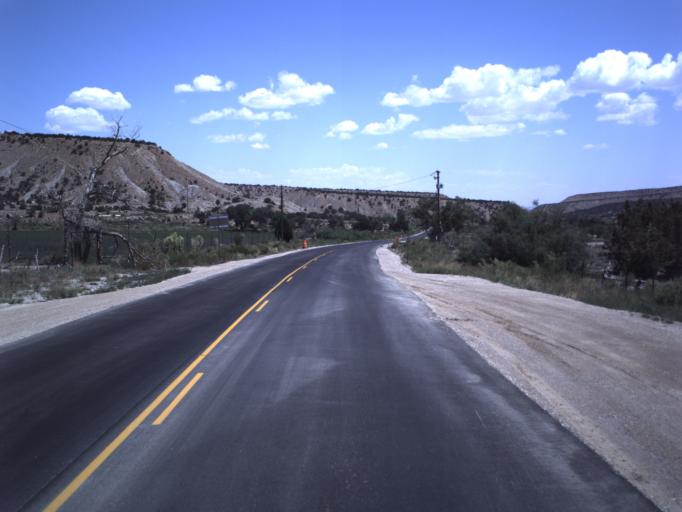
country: US
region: Utah
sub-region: Emery County
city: Orangeville
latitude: 39.2763
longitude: -111.1741
